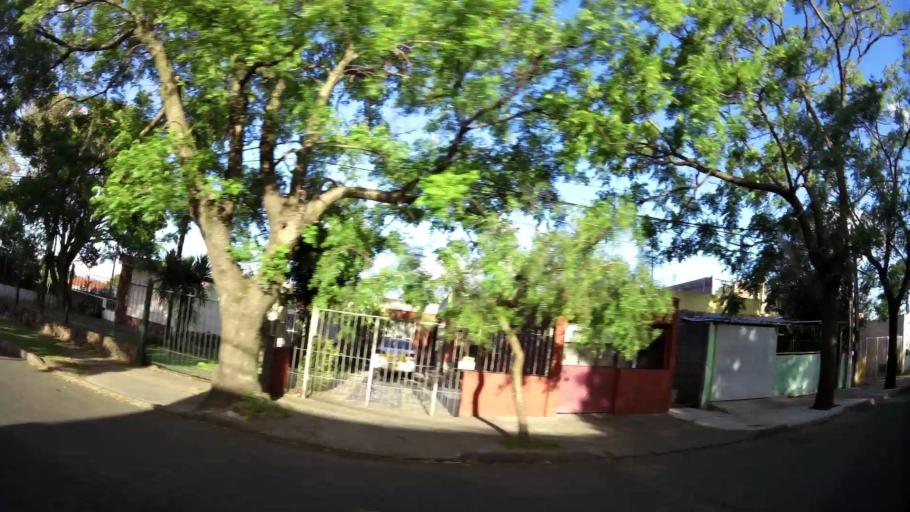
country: UY
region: Montevideo
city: Montevideo
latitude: -34.8783
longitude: -56.2659
